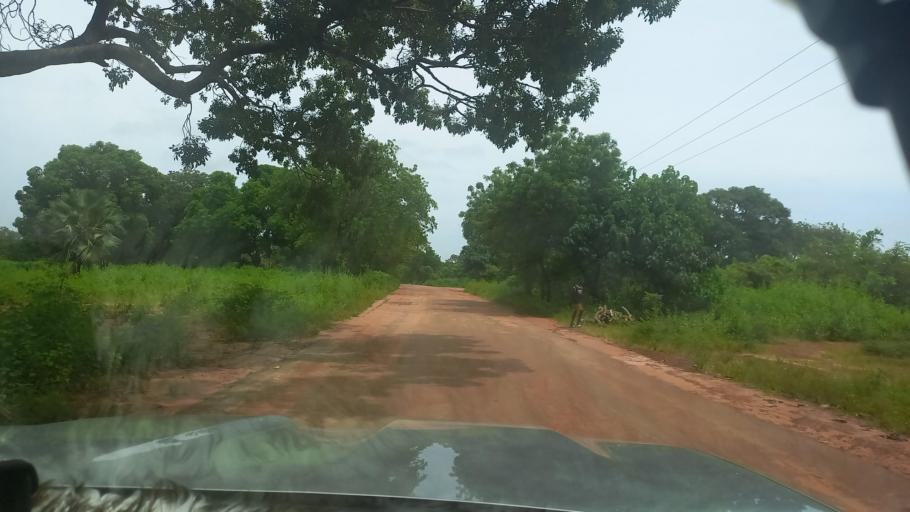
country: SN
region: Kolda
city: Marsassoum
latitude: 12.9086
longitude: -16.0130
